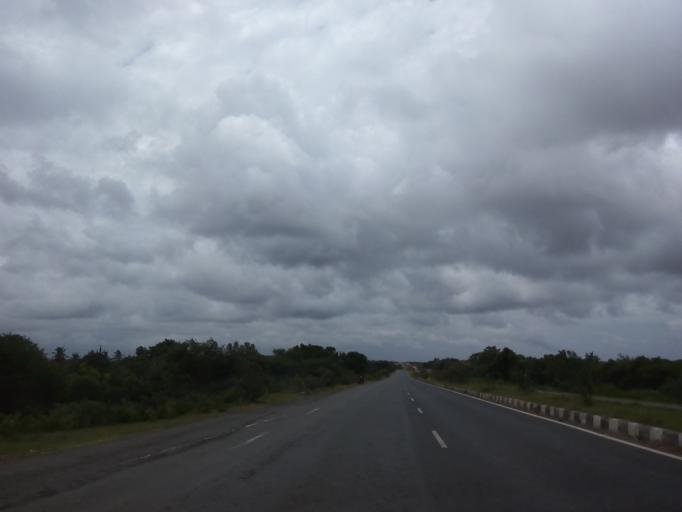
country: IN
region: Karnataka
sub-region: Haveri
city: Byadgi
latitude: 14.6644
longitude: 75.5618
